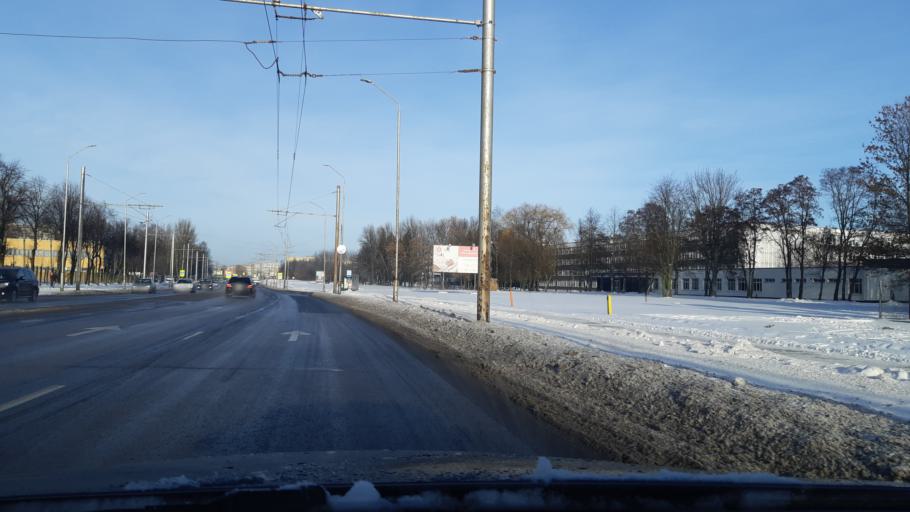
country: LT
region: Kauno apskritis
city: Dainava (Kaunas)
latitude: 54.9186
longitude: 23.9841
